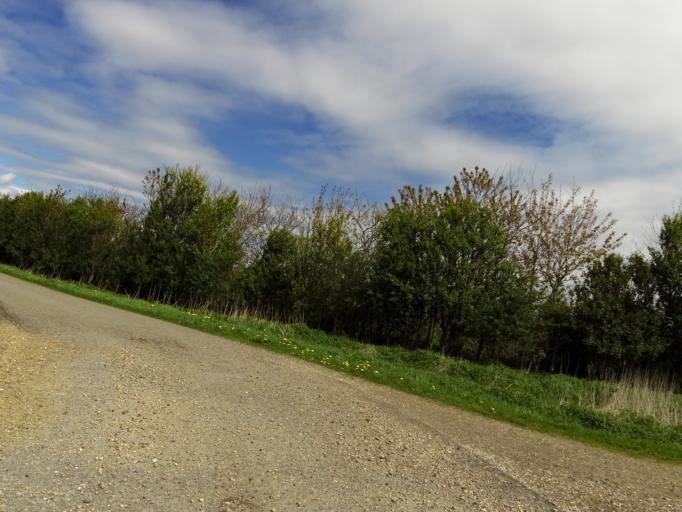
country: DK
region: South Denmark
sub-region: Haderslev Kommune
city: Gram
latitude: 55.2549
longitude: 9.0417
